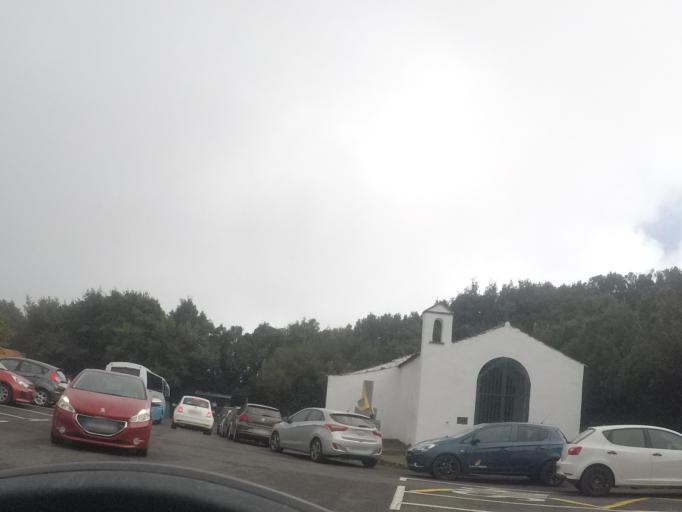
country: ES
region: Canary Islands
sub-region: Provincia de Santa Cruz de Tenerife
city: Tegueste
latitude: 28.5309
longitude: -16.2799
